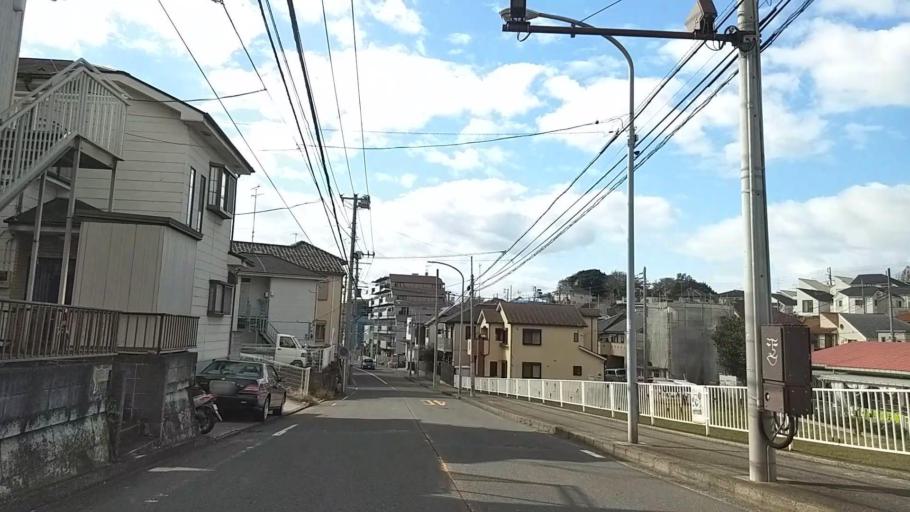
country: JP
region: Kanagawa
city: Yokohama
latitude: 35.5078
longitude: 139.6520
